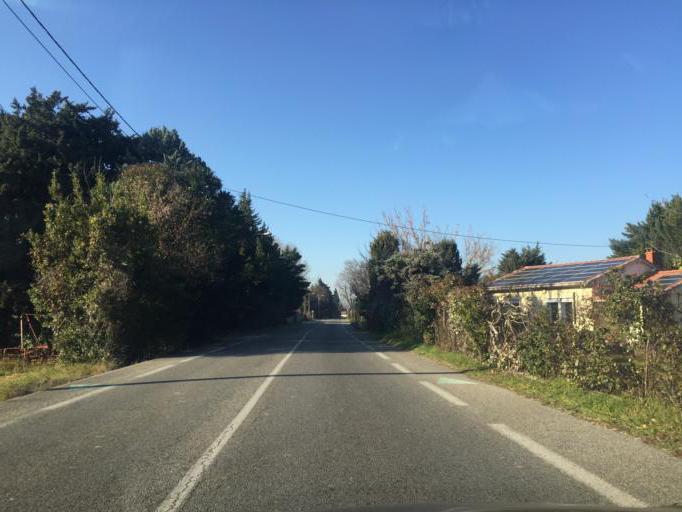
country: FR
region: Provence-Alpes-Cote d'Azur
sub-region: Departement du Vaucluse
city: Montfavet
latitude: 43.9299
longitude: 4.8649
